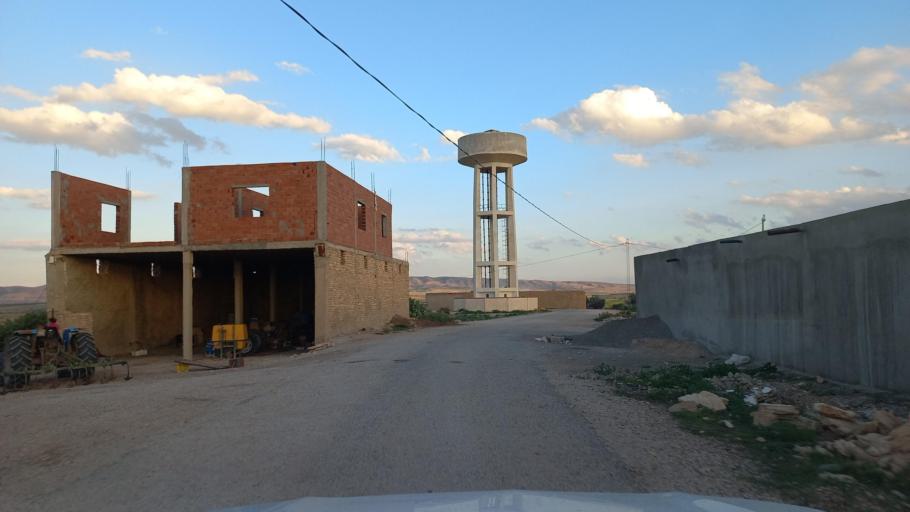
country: TN
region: Al Qasrayn
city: Sbiba
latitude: 35.3726
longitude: 9.0623
